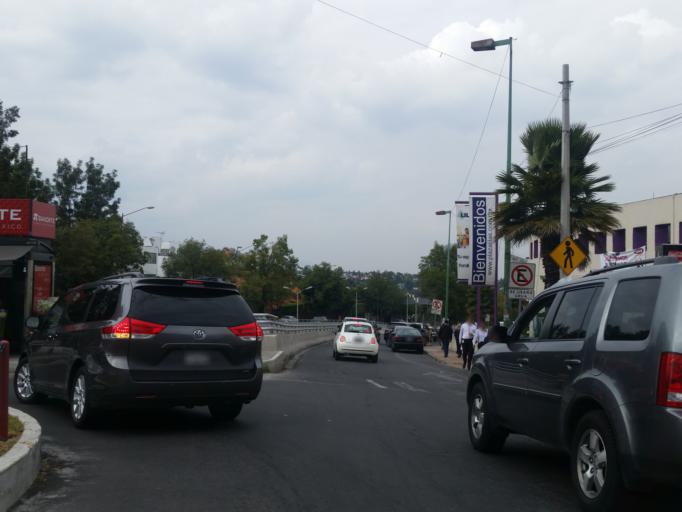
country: MX
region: Mexico City
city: Col. Bosques de las Lomas
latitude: 19.3870
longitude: -99.2479
